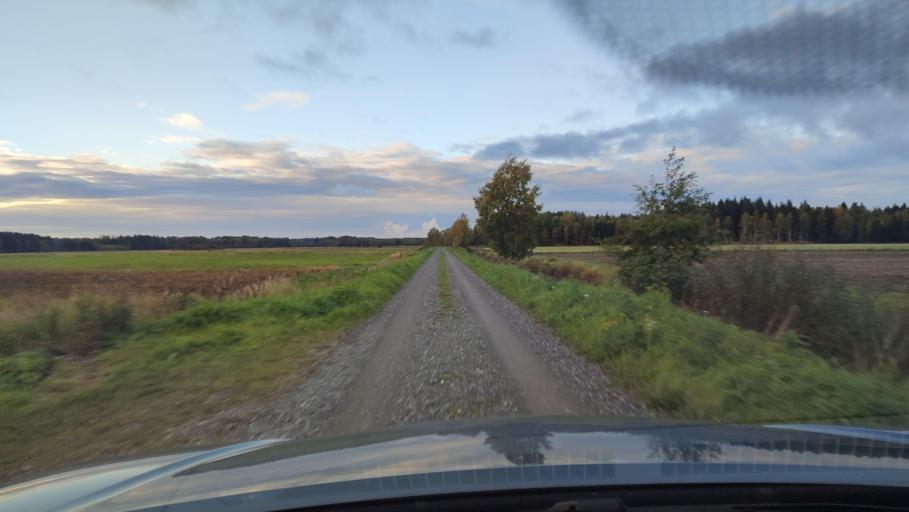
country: FI
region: Ostrobothnia
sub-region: Sydosterbotten
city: Kristinestad
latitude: 62.2409
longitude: 21.4546
